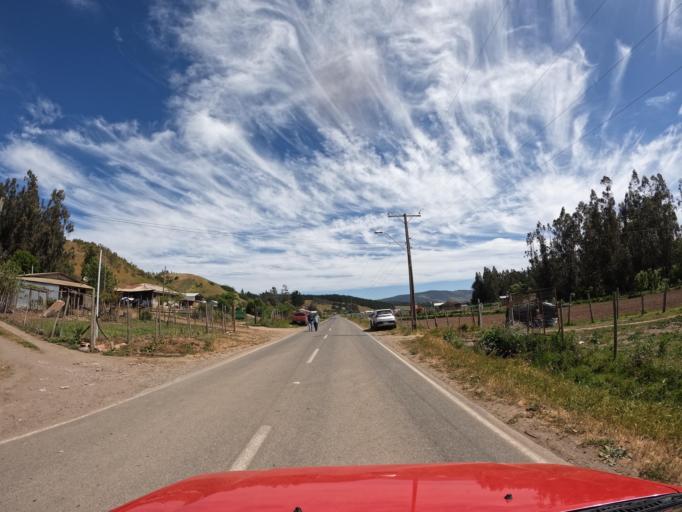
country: CL
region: Maule
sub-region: Provincia de Talca
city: Constitucion
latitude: -35.0166
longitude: -72.0384
